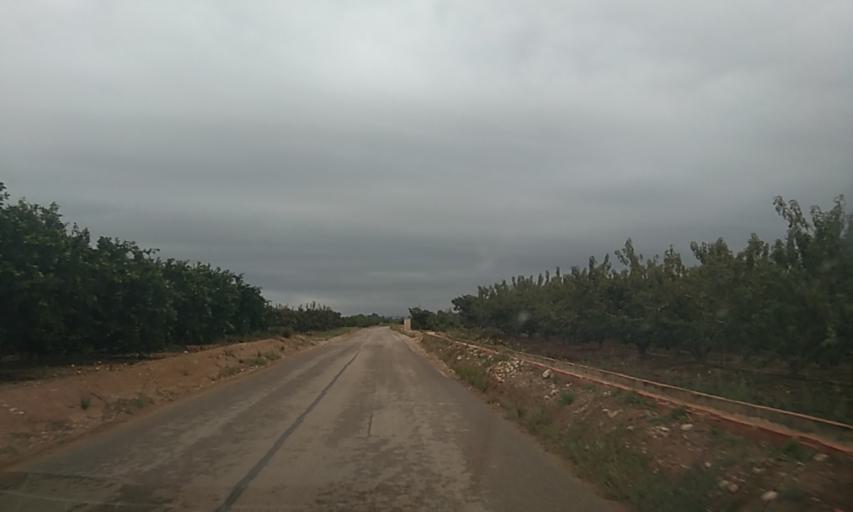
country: ES
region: Valencia
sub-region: Provincia de Valencia
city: Benimodo
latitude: 39.1888
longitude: -0.5398
